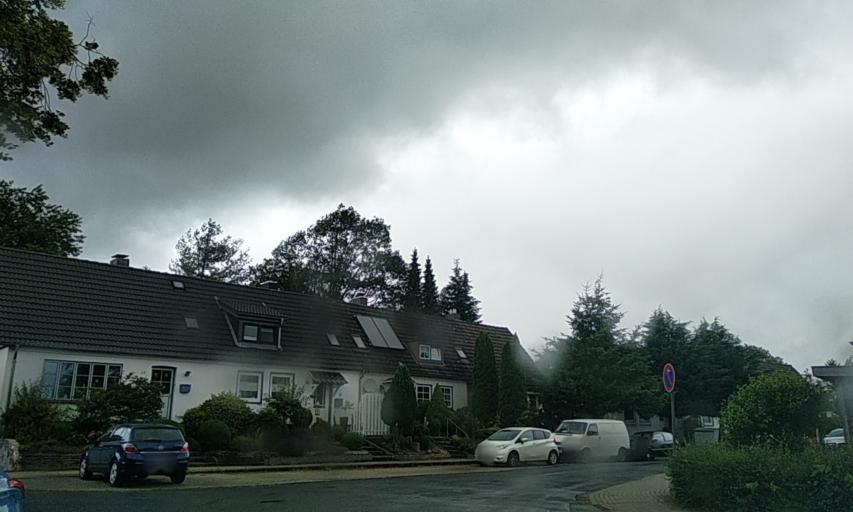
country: DE
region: Schleswig-Holstein
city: Schleswig
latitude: 54.5267
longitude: 9.5514
